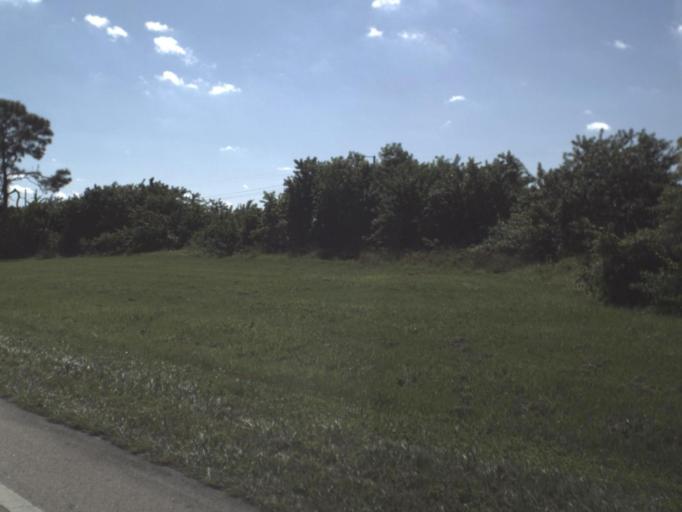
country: US
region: Florida
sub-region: Collier County
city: Immokalee
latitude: 26.5000
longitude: -81.4914
